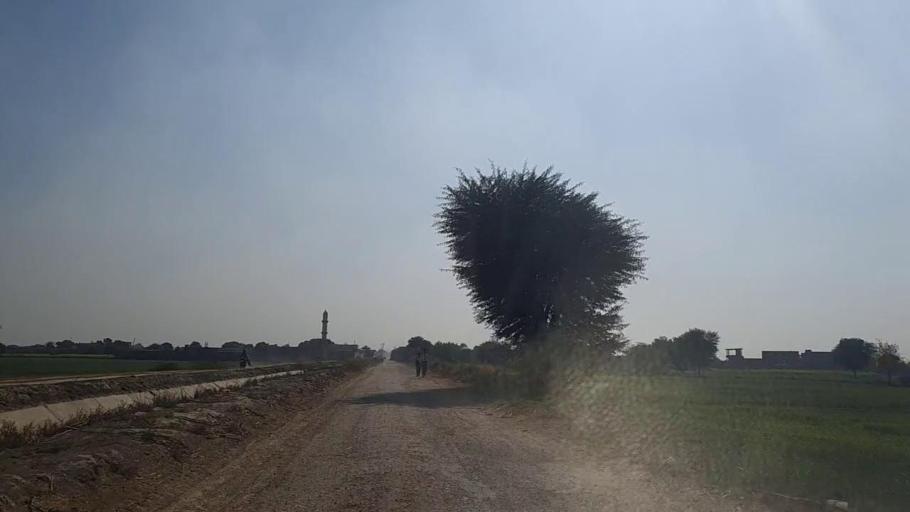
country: PK
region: Sindh
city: Shahpur Chakar
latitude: 26.1920
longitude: 68.5835
